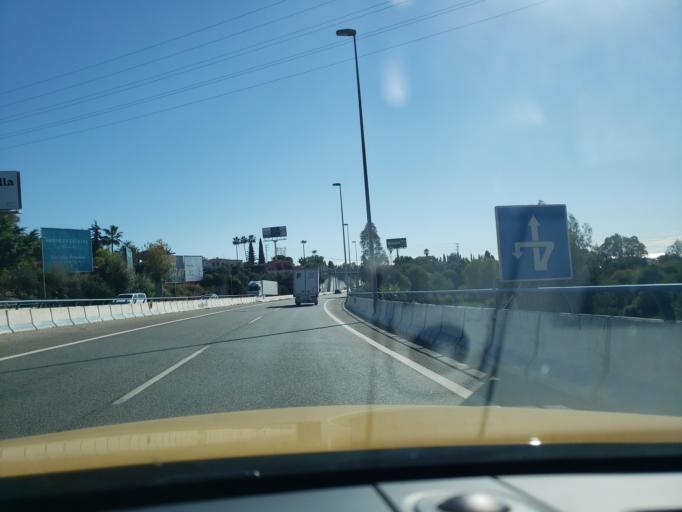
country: ES
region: Andalusia
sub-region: Provincia de Malaga
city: Marbella
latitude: 36.5185
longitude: -4.8658
